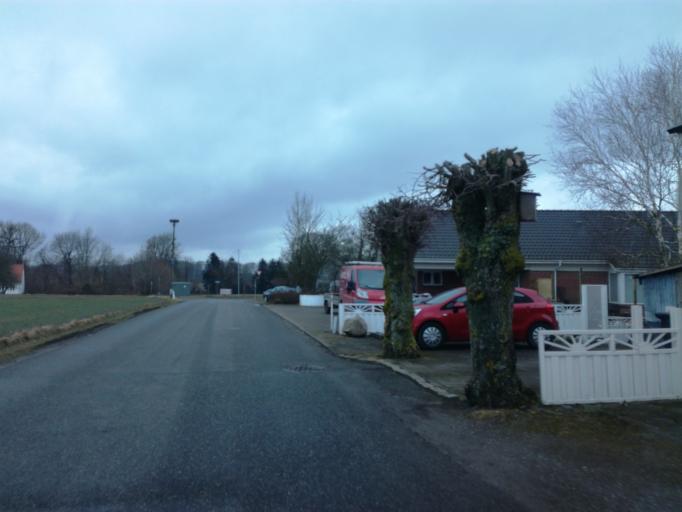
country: DK
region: South Denmark
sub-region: Vejle Kommune
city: Borkop
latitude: 55.6045
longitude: 9.6408
